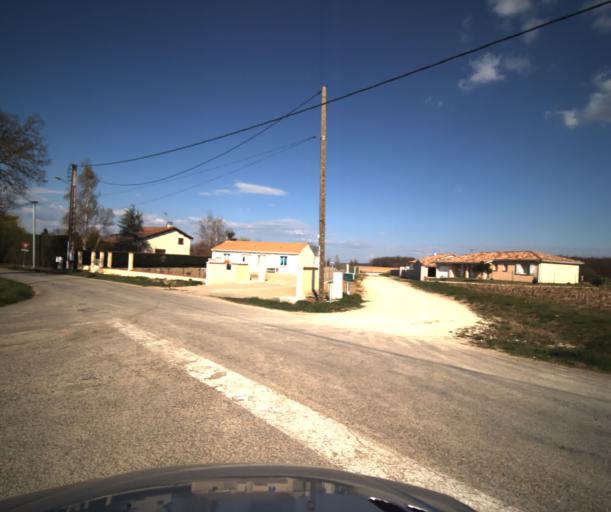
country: FR
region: Midi-Pyrenees
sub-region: Departement du Tarn-et-Garonne
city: Bressols
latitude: 43.9585
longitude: 1.3045
